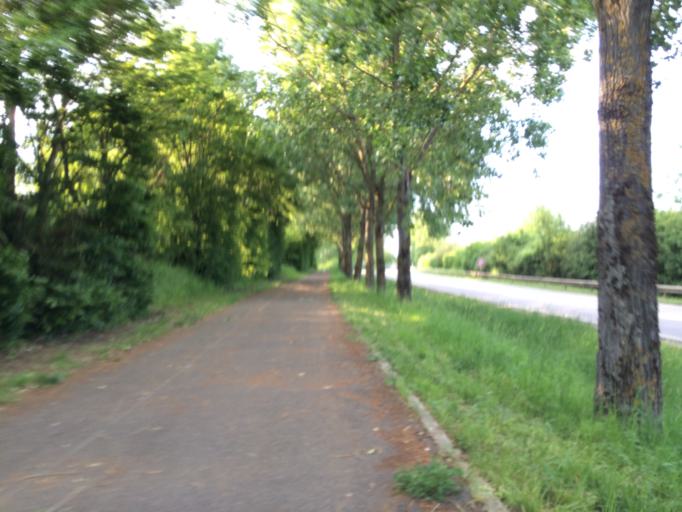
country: FR
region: Ile-de-France
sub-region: Departement de l'Essonne
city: Lisses
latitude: 48.6091
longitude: 2.4244
